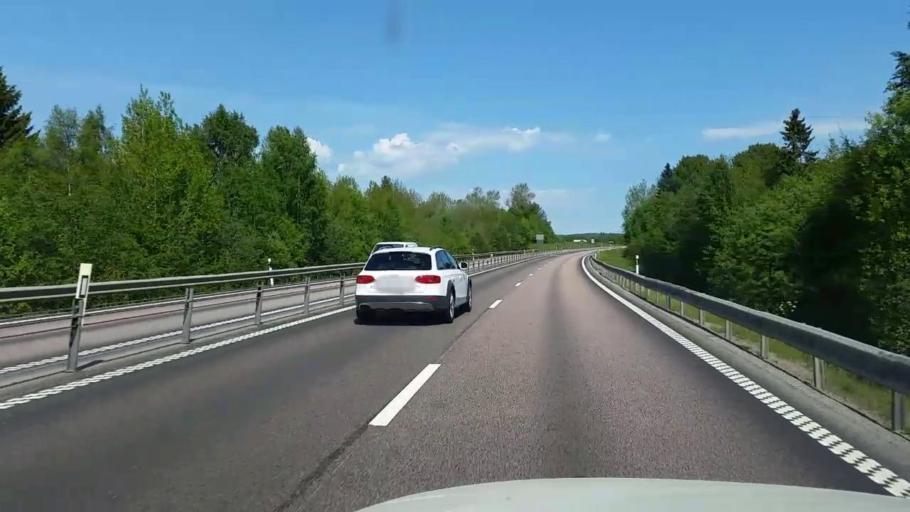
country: SE
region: Gaevleborg
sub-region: Hudiksvalls Kommun
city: Hudiksvall
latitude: 61.7508
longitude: 17.0802
